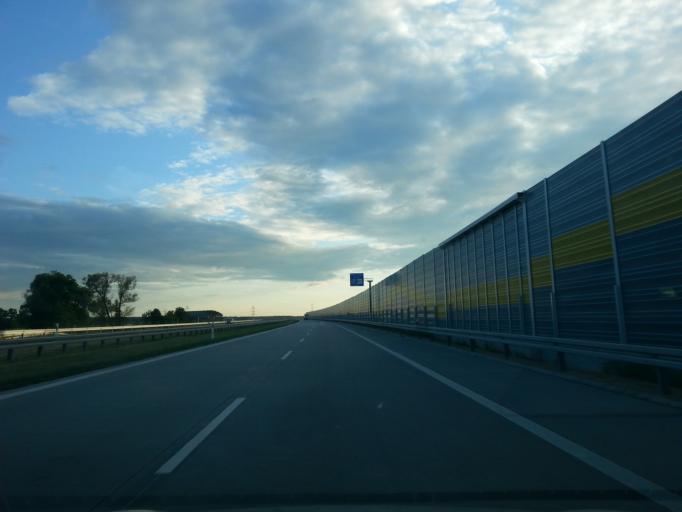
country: PL
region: Lodz Voivodeship
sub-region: Powiat sieradzki
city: Zloczew
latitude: 51.3918
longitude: 18.5784
